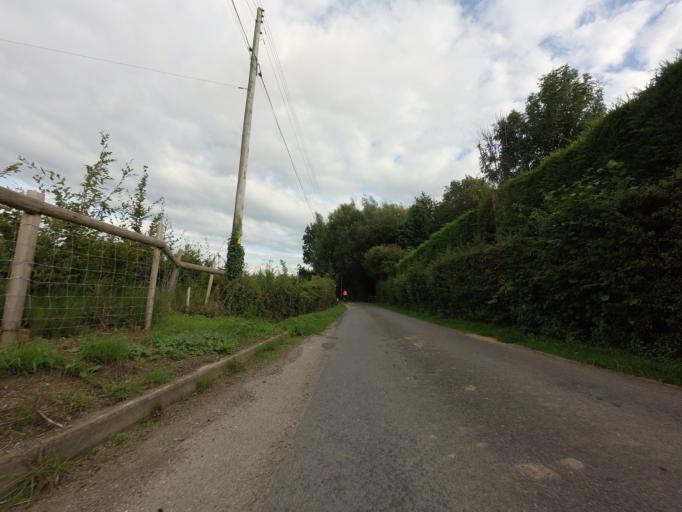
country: GB
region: England
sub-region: Kent
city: Staplehurst
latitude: 51.1992
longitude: 0.5689
